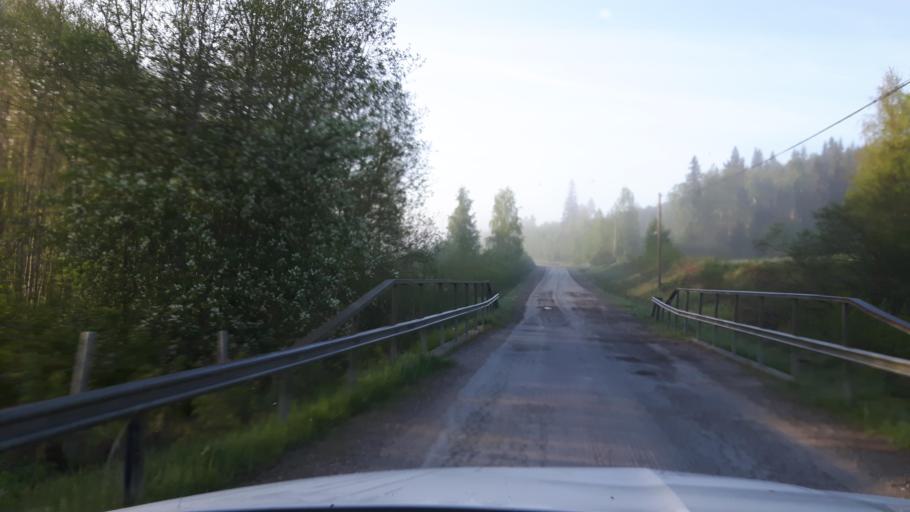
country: SE
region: Gaevleborg
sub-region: Ljusdals Kommun
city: Farila
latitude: 62.0657
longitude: 15.7852
